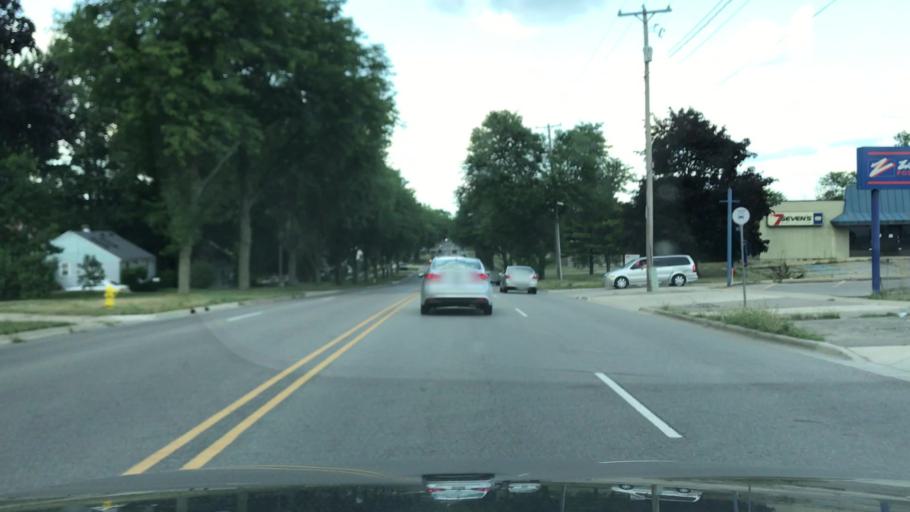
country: US
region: Michigan
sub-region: Kent County
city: Grand Rapids
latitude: 42.9860
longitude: -85.6399
